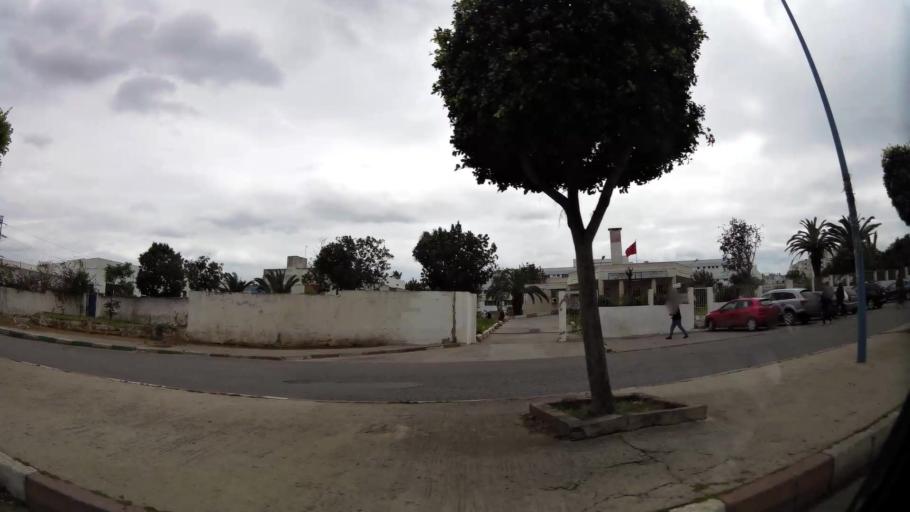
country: MA
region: Grand Casablanca
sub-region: Casablanca
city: Casablanca
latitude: 33.5902
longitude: -7.5523
